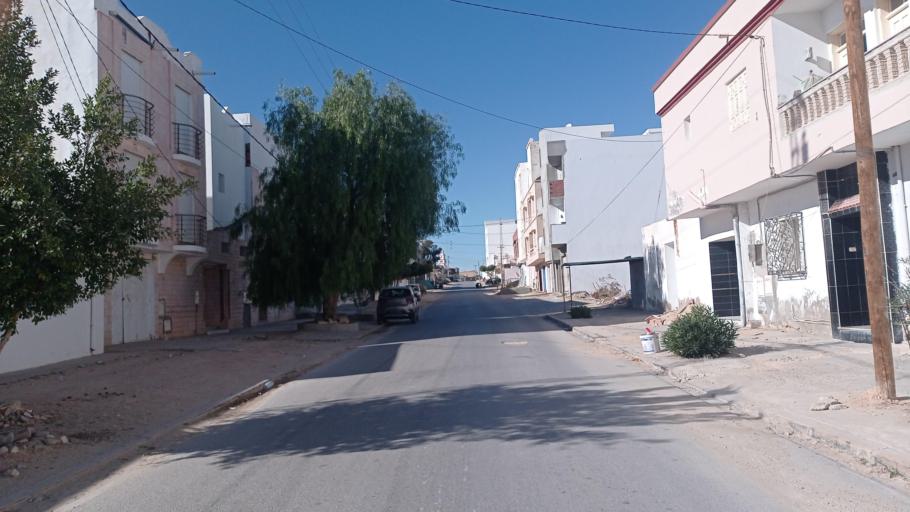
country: TN
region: Qabis
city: Gabes
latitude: 33.8459
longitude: 10.1118
